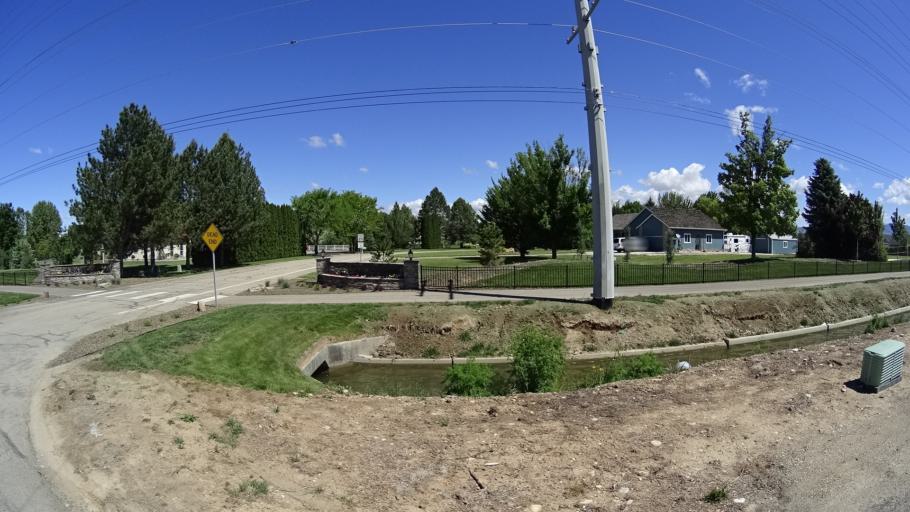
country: US
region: Idaho
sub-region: Ada County
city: Meridian
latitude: 43.6484
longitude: -116.3804
